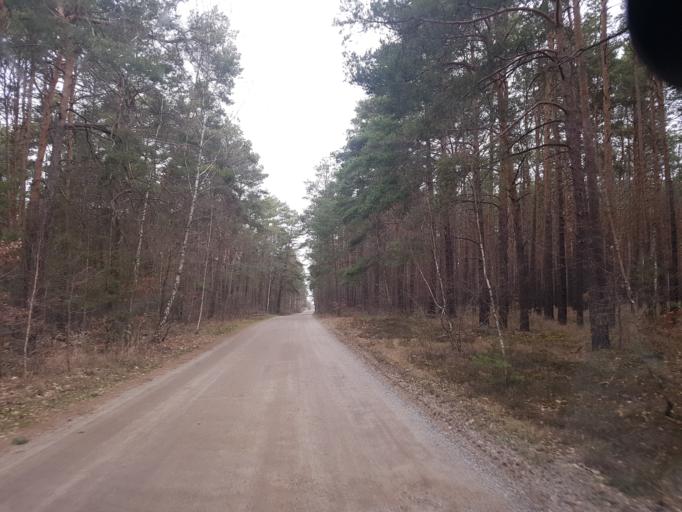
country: DE
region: Brandenburg
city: Finsterwalde
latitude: 51.6542
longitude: 13.6771
